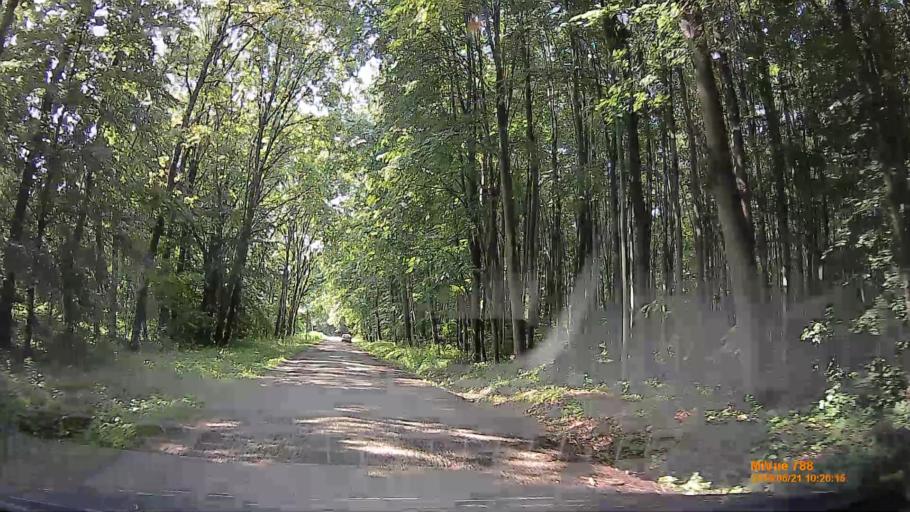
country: HU
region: Baranya
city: Buekkoesd
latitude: 46.1970
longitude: 17.9704
